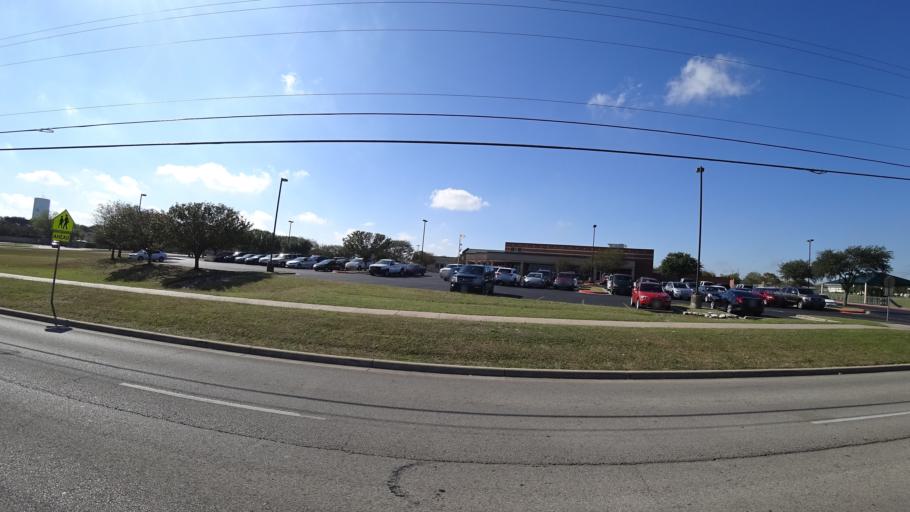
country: US
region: Texas
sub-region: Travis County
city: Windemere
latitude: 30.4431
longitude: -97.6441
